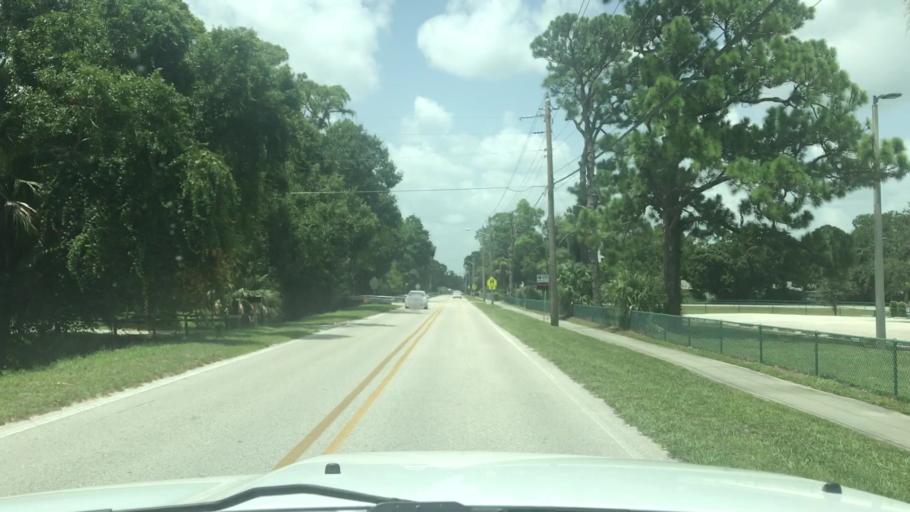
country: US
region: Florida
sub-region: Indian River County
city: Vero Beach South
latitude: 27.6312
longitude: -80.4248
